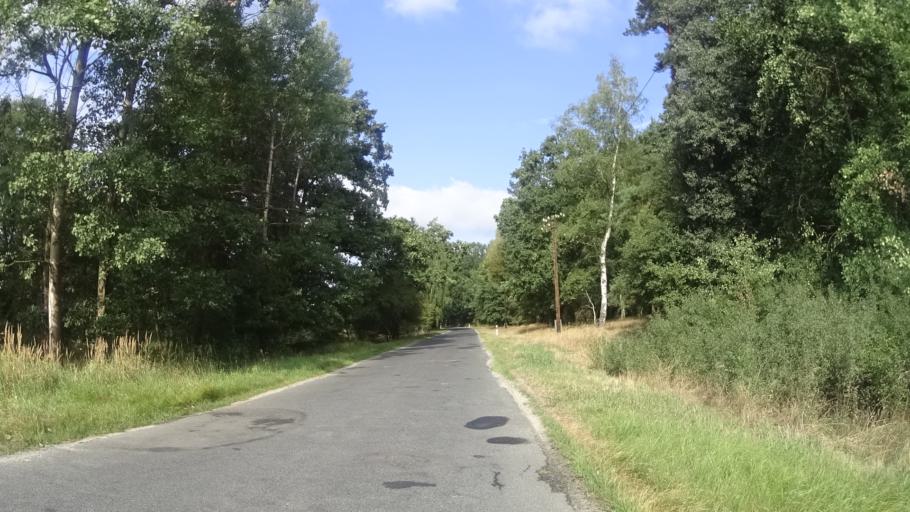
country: PL
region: Lubusz
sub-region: Powiat zarski
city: Przewoz
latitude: 51.4913
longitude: 14.8749
